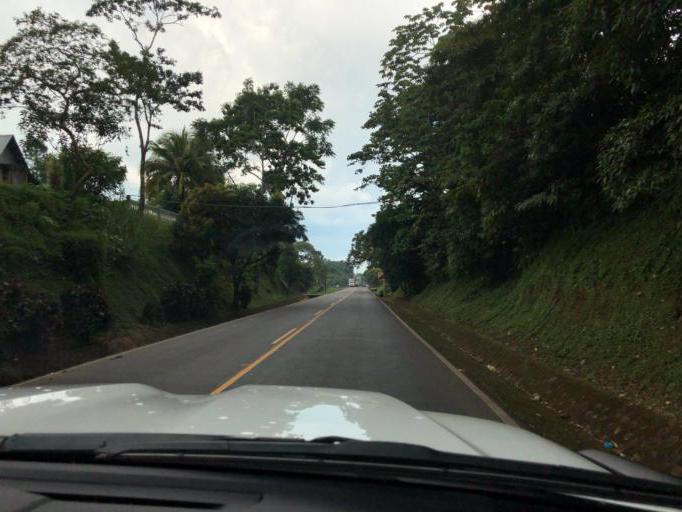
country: NI
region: Chontales
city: Villa Sandino
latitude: 11.9969
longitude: -84.7861
